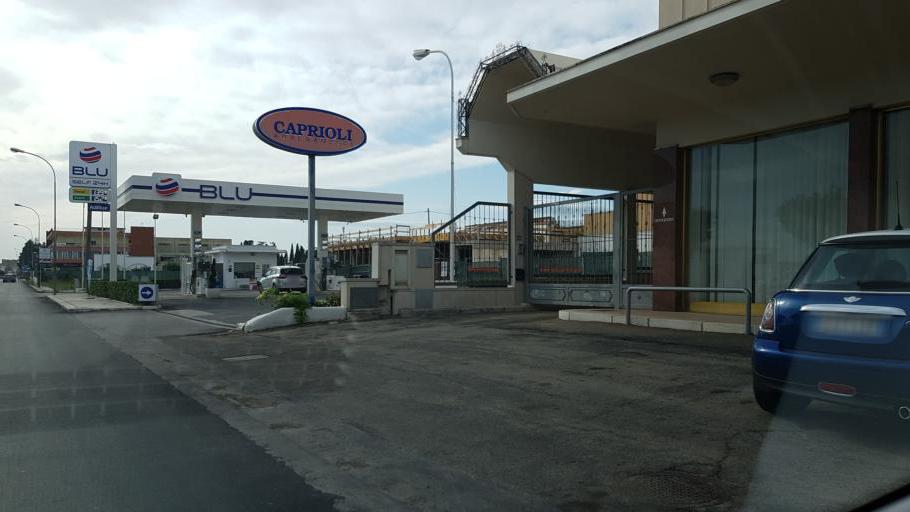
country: IT
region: Apulia
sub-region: Provincia di Brindisi
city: Mesagne
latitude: 40.5669
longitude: 17.8184
